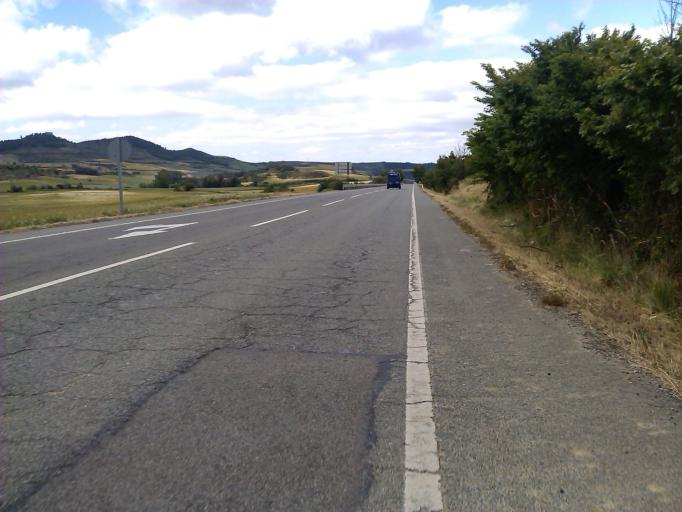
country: ES
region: Navarre
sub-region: Provincia de Navarra
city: Obanos
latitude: 42.6909
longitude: -1.7934
